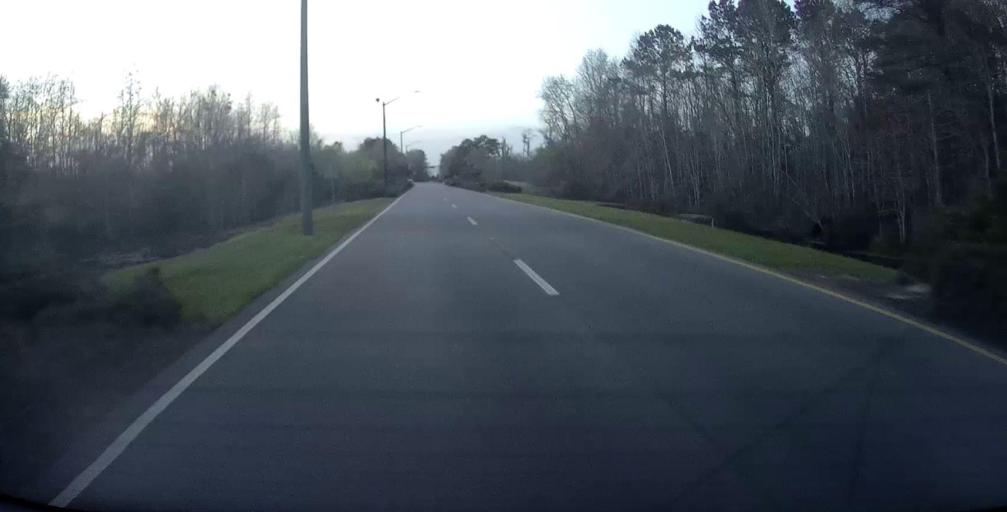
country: US
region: Georgia
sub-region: Chatham County
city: Pooler
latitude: 32.1353
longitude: -81.2164
